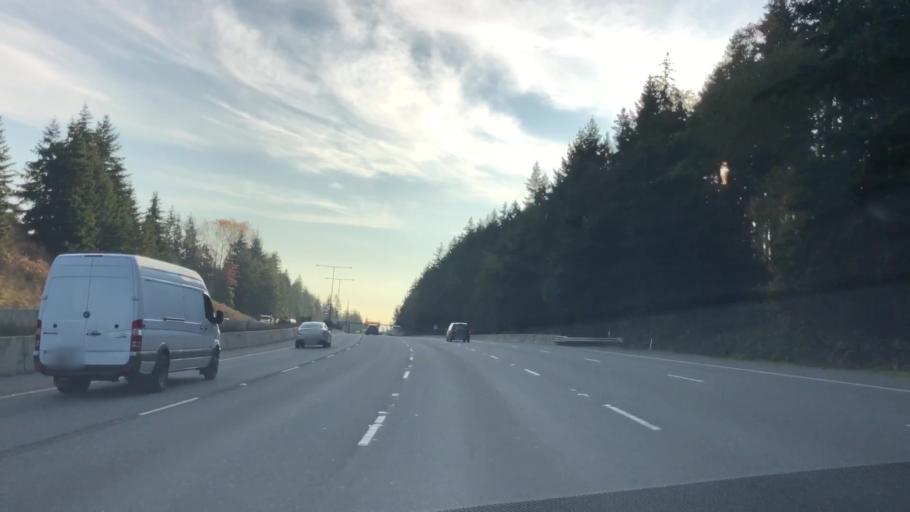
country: US
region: Washington
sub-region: Snohomish County
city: Martha Lake
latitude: 47.8233
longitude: -122.2510
